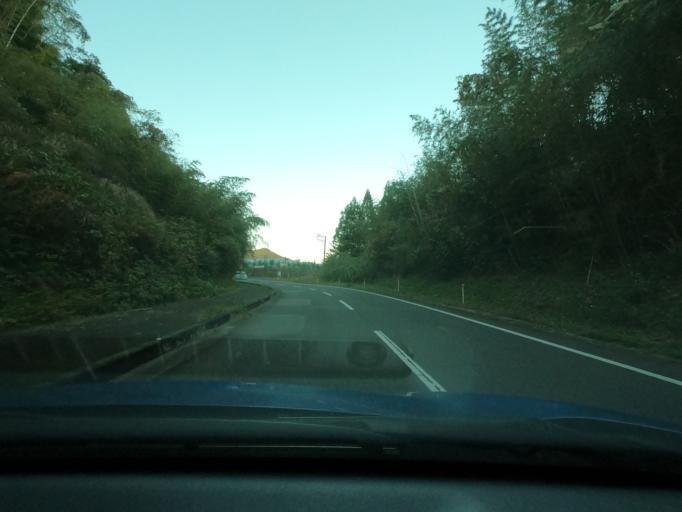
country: JP
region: Kagoshima
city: Satsumasendai
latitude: 31.8181
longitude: 130.4836
